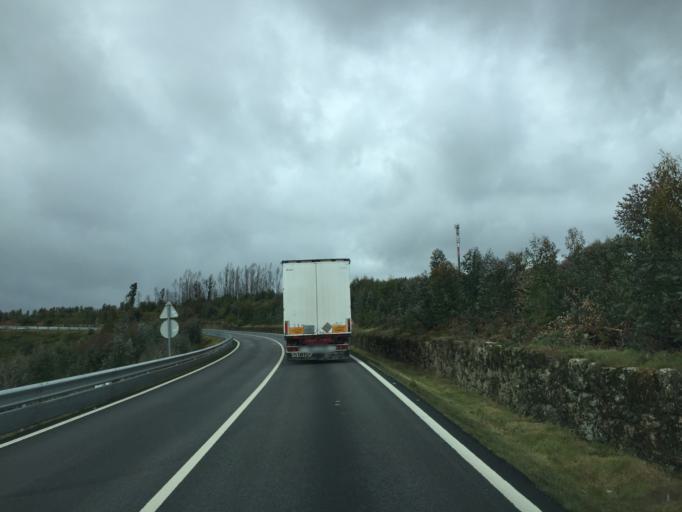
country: PT
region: Coimbra
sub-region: Oliveira do Hospital
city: Oliveira do Hospital
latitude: 40.3238
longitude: -7.9281
